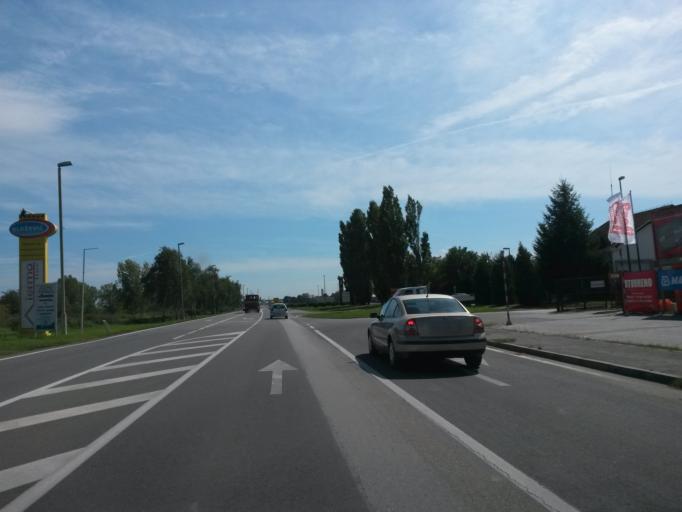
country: HR
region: Vukovarsko-Srijemska
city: Vinkovci
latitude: 45.2721
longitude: 18.8079
